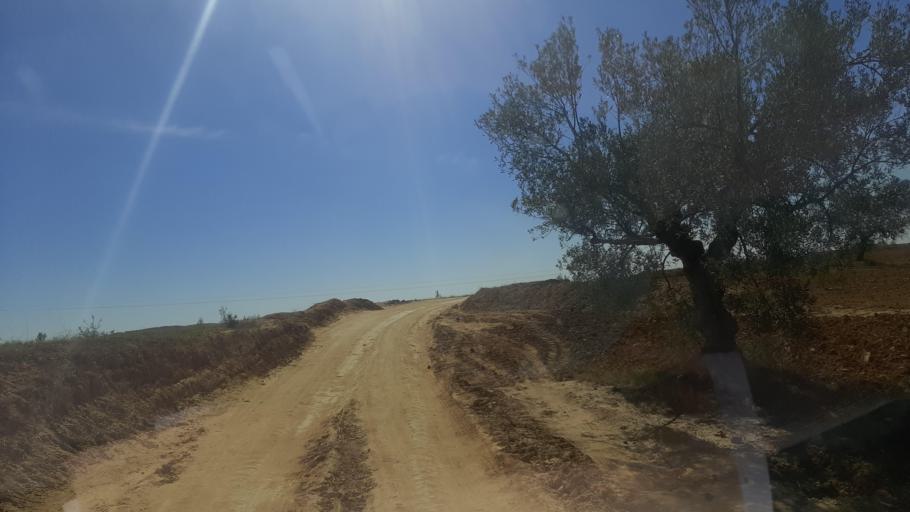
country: TN
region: Safaqis
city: Sfax
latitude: 34.7906
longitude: 10.5316
